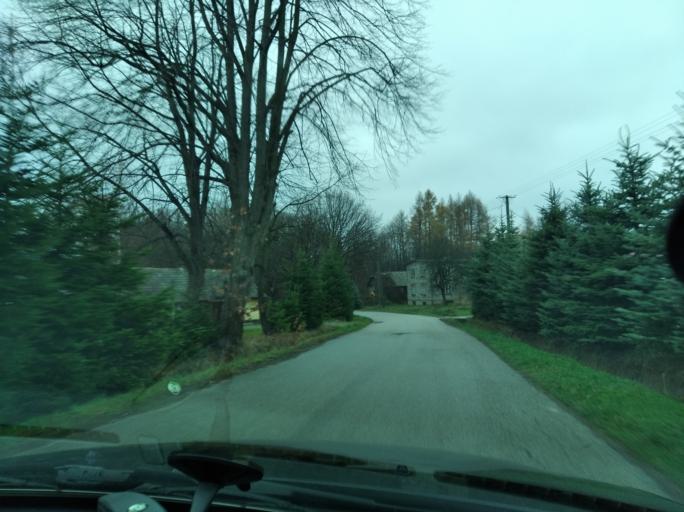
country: PL
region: Subcarpathian Voivodeship
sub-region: Powiat przeworski
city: Jawornik Polski
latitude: 49.9000
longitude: 22.2770
